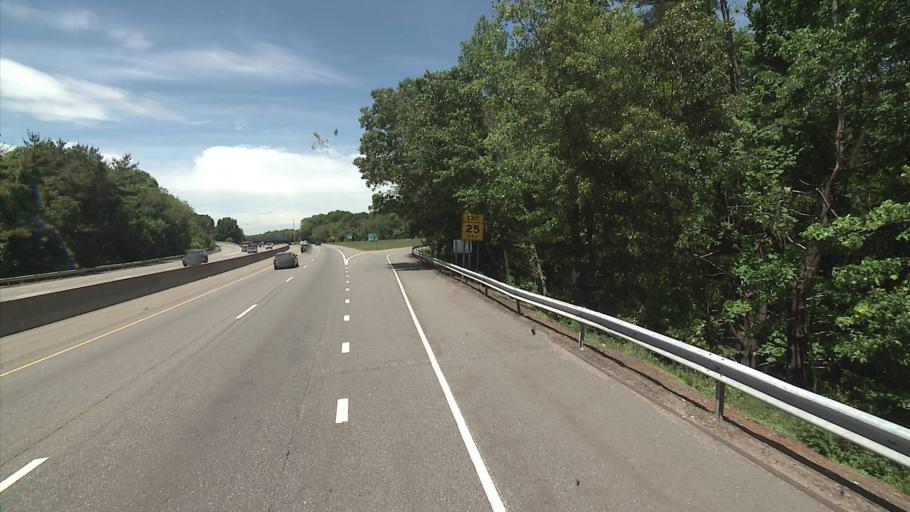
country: US
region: Connecticut
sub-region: New Haven County
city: Madison
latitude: 41.2903
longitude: -72.5654
